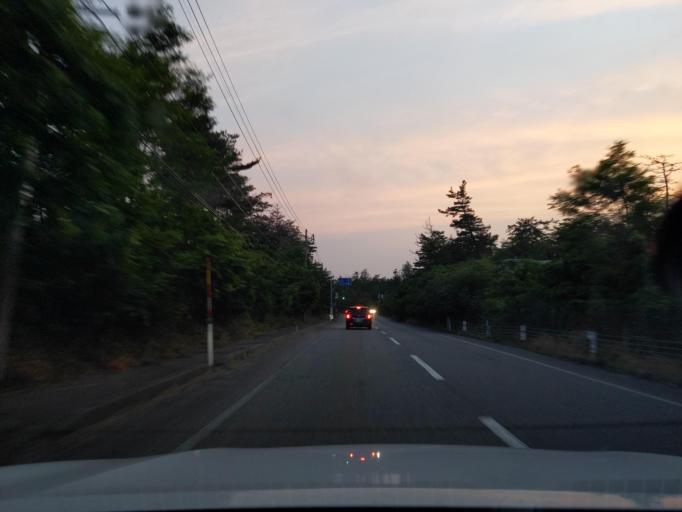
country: JP
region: Niigata
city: Kashiwazaki
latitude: 37.4175
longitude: 138.5975
